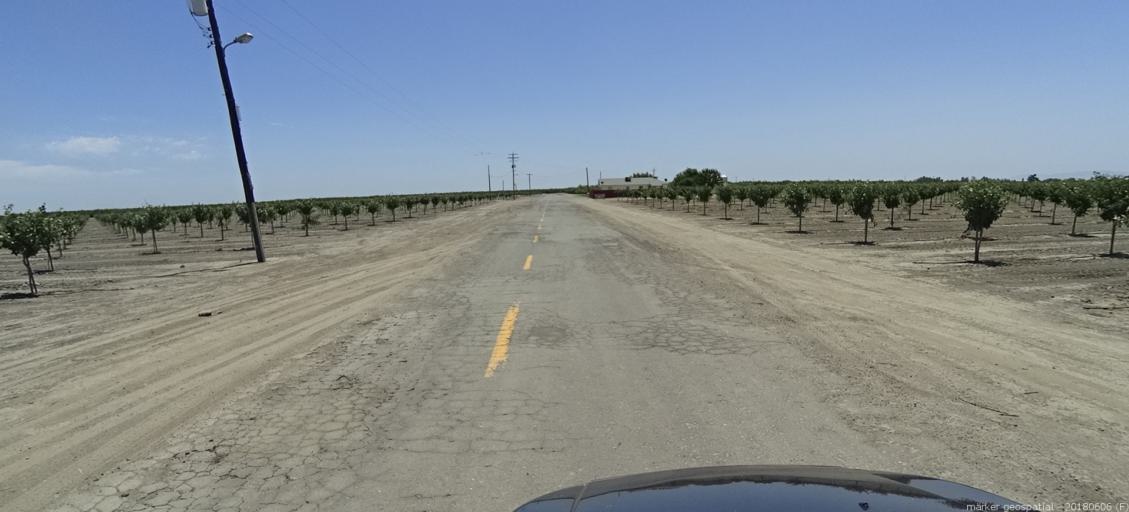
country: US
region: California
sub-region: Fresno County
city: Firebaugh
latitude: 36.8350
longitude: -120.3817
